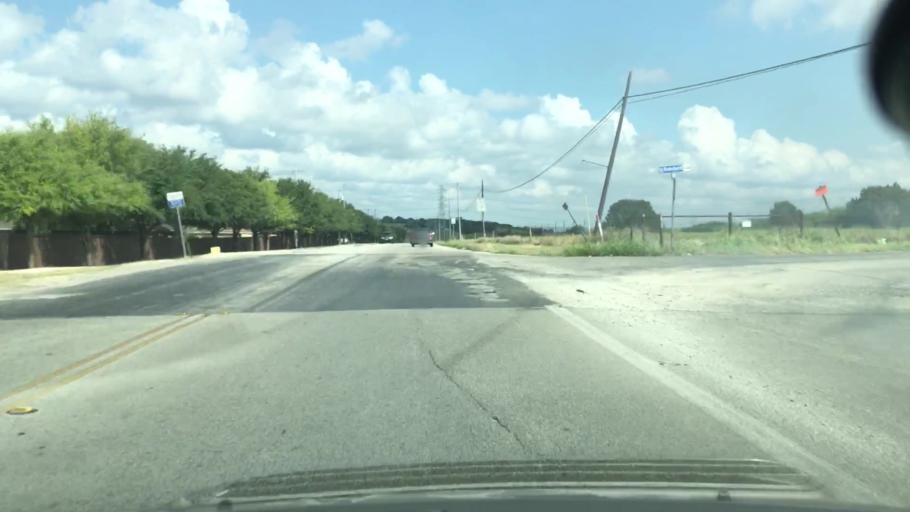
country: US
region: Texas
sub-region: Guadalupe County
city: Northcliff
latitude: 29.6019
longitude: -98.2616
